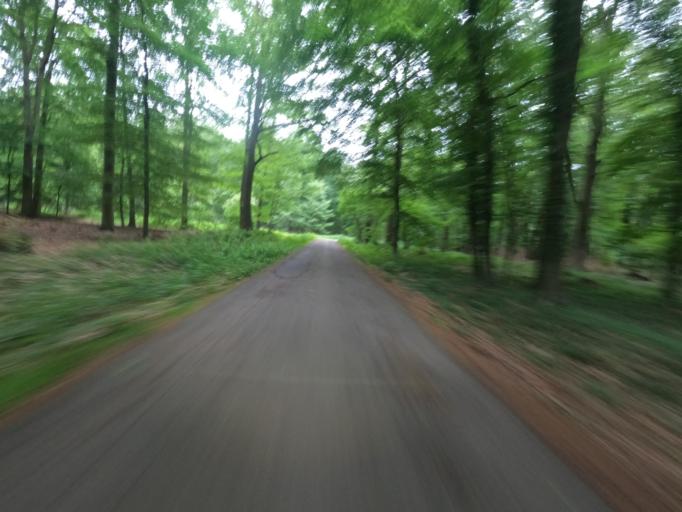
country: DE
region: North Rhine-Westphalia
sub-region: Regierungsbezirk Koln
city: Wassenberg
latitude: 51.1205
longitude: 6.1192
